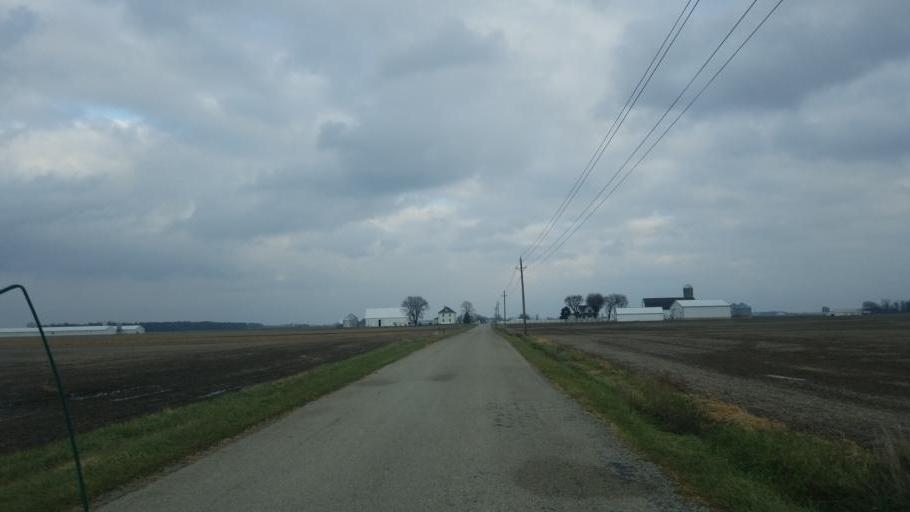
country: US
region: Ohio
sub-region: Mercer County
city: Fort Recovery
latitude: 40.5135
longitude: -84.8307
